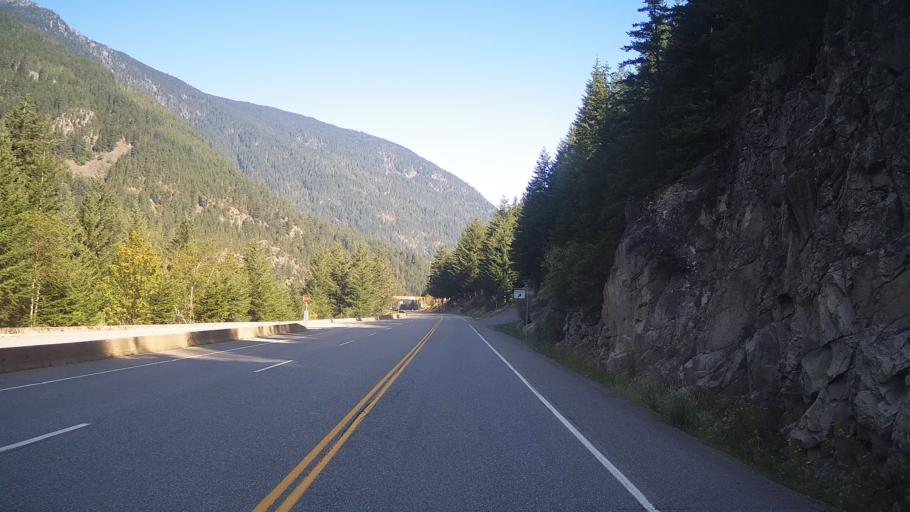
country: CA
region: British Columbia
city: Hope
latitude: 49.7780
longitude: -121.4422
